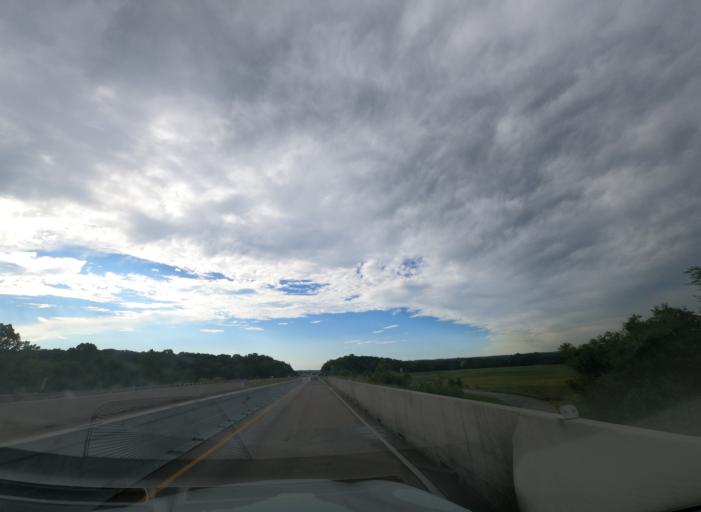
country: US
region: Missouri
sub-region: Sainte Genevieve County
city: Sainte Genevieve
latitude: 37.9943
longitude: -90.2084
